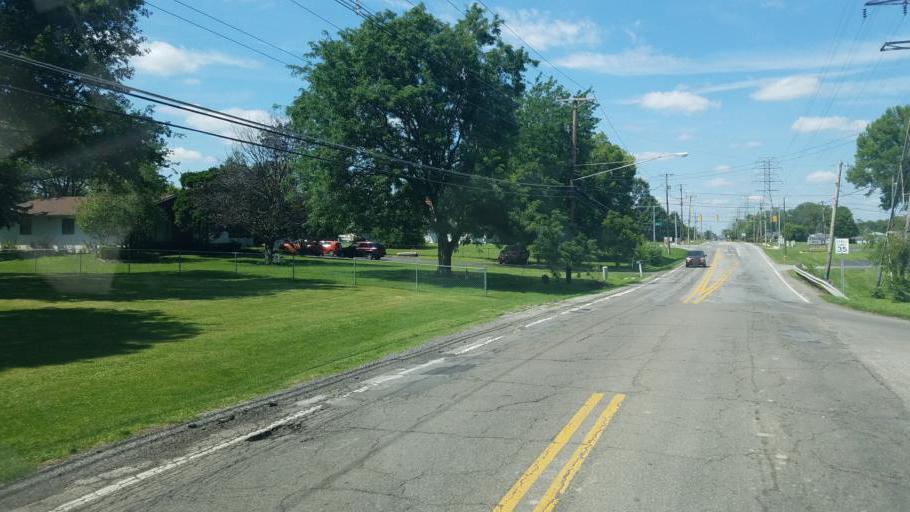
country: US
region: Ohio
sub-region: Franklin County
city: Obetz
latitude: 39.8803
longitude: -82.9879
